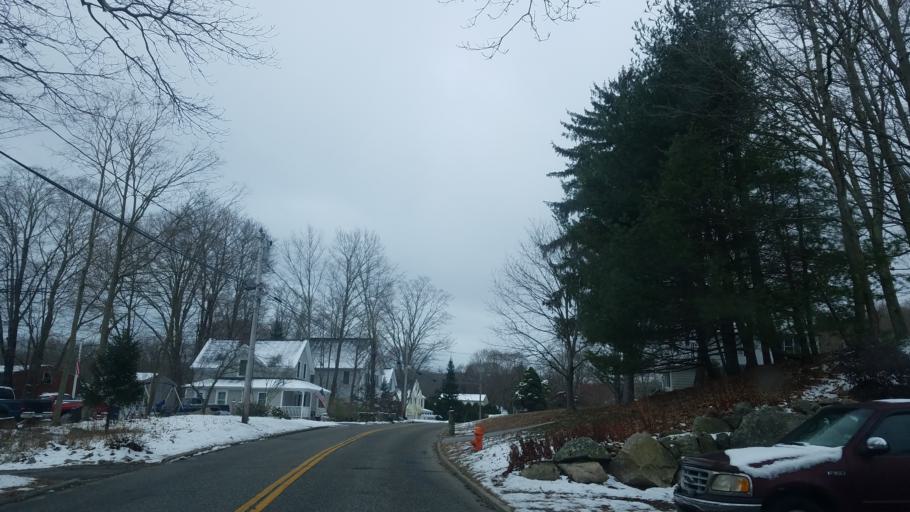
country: US
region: Connecticut
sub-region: New London County
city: Central Waterford
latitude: 41.3507
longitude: -72.1452
